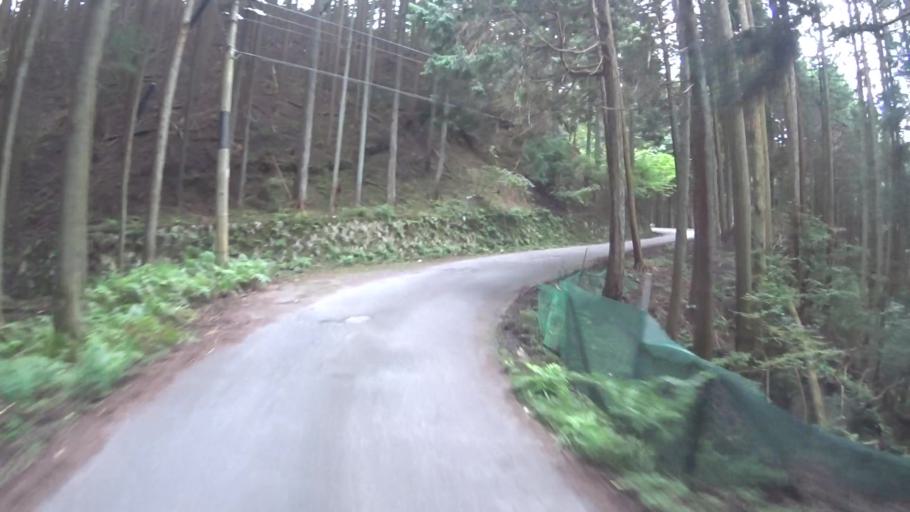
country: JP
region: Kyoto
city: Uji
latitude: 34.8512
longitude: 135.9414
